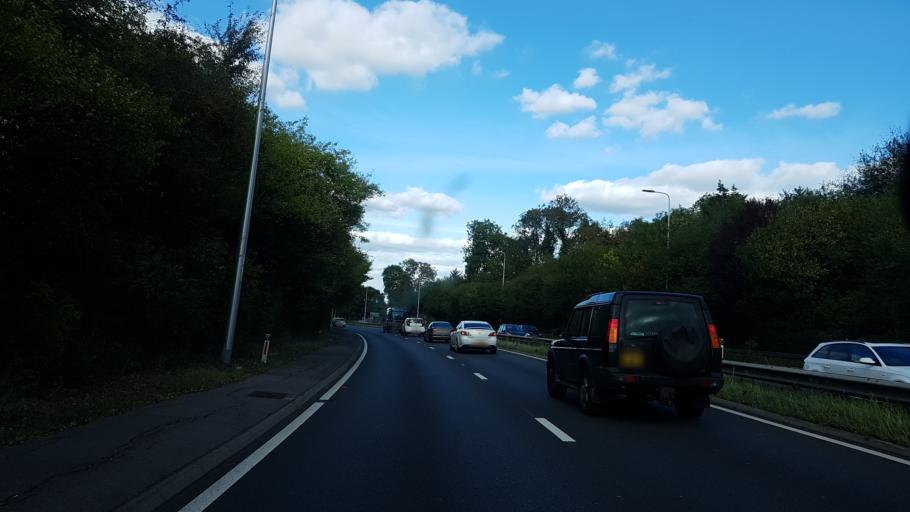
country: GB
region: England
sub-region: Surrey
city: Guildford
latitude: 51.2352
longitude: -0.6026
